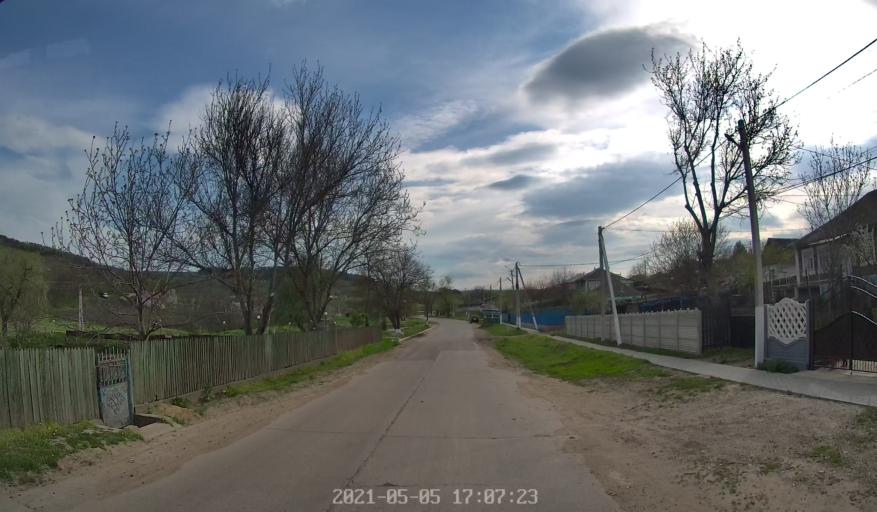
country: MD
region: Chisinau
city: Vadul lui Voda
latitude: 47.0133
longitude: 29.1349
